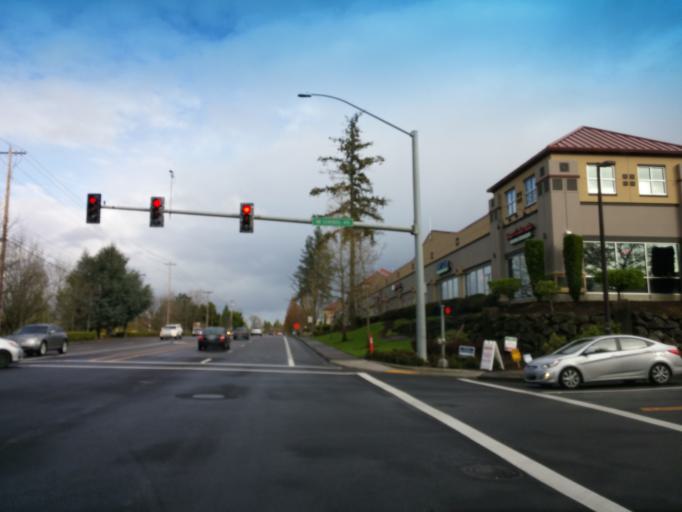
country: US
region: Oregon
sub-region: Washington County
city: Oak Hills
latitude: 45.5182
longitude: -122.8441
